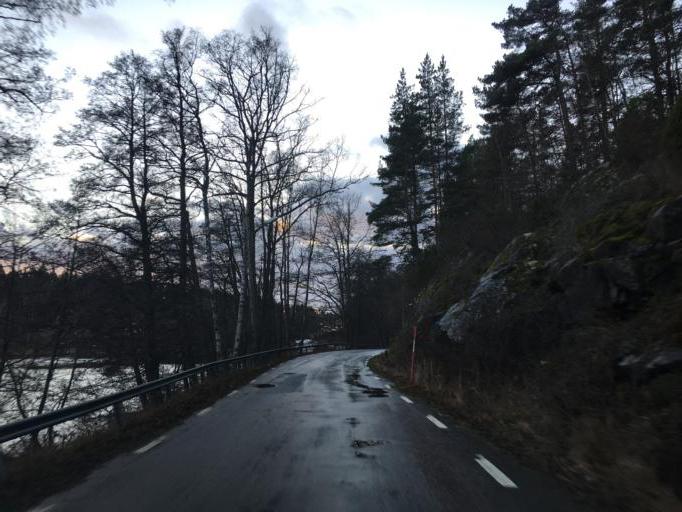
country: SE
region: Kalmar
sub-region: Vasterviks Kommun
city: Vaestervik
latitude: 57.5789
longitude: 16.5151
